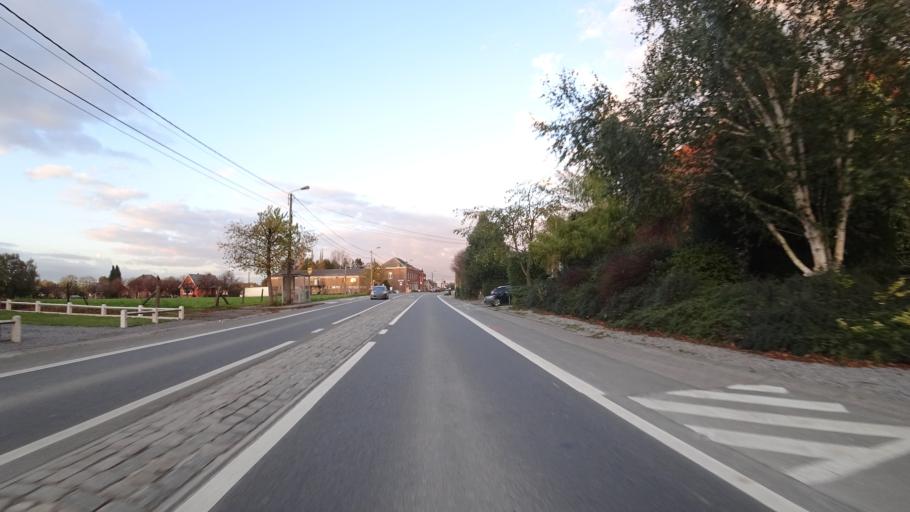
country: BE
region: Wallonia
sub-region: Province de Namur
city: Gembloux
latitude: 50.5346
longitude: 4.7812
